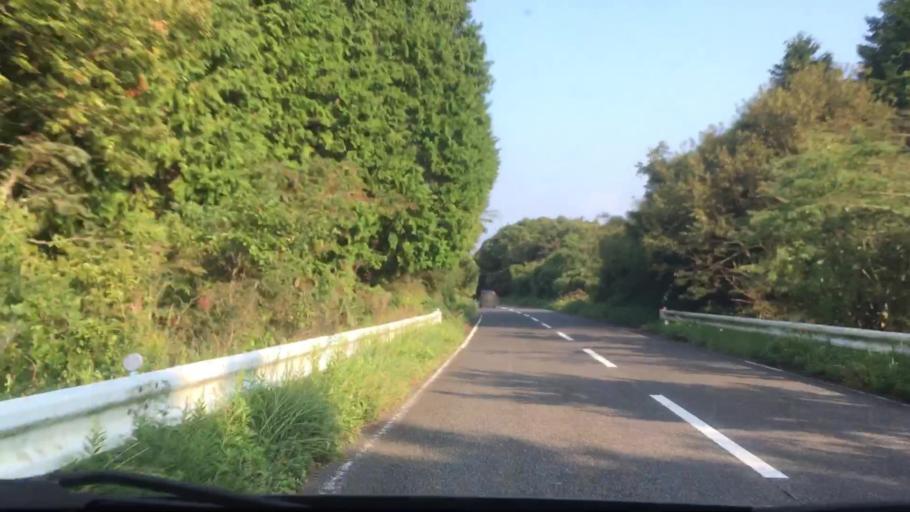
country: JP
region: Nagasaki
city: Sasebo
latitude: 33.0300
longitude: 129.6899
